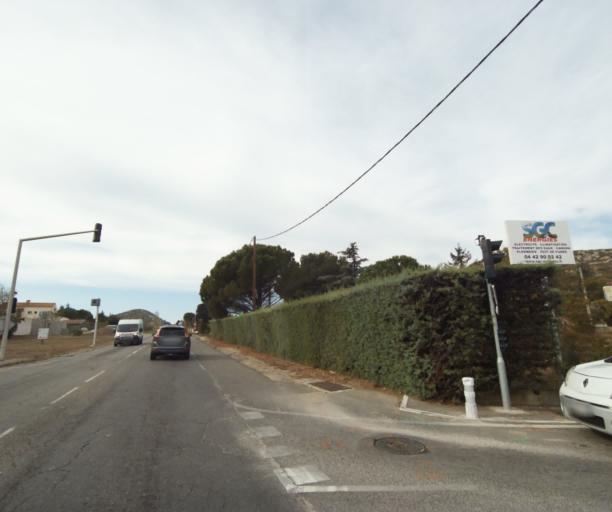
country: FR
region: Provence-Alpes-Cote d'Azur
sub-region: Departement des Bouches-du-Rhone
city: Le Rove
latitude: 43.3674
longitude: 5.2479
